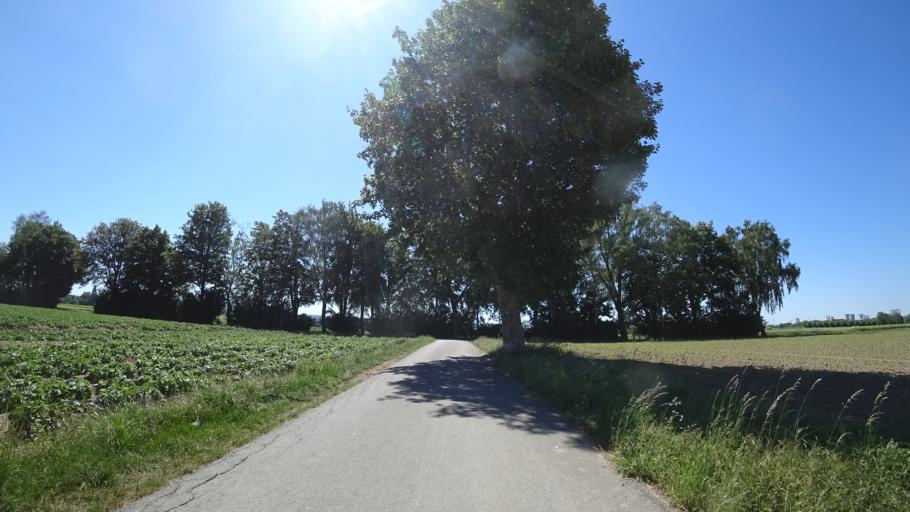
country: DE
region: North Rhine-Westphalia
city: Erwitte
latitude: 51.6215
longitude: 8.3616
